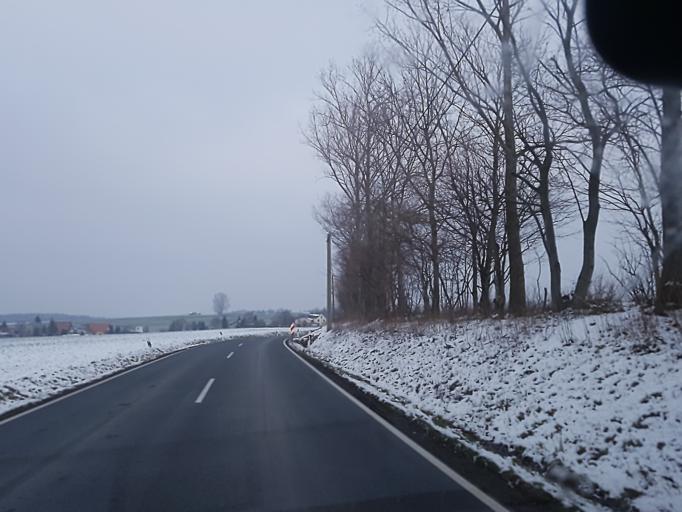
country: DE
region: Saxony
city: Bockelwitz
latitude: 51.2059
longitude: 12.9833
